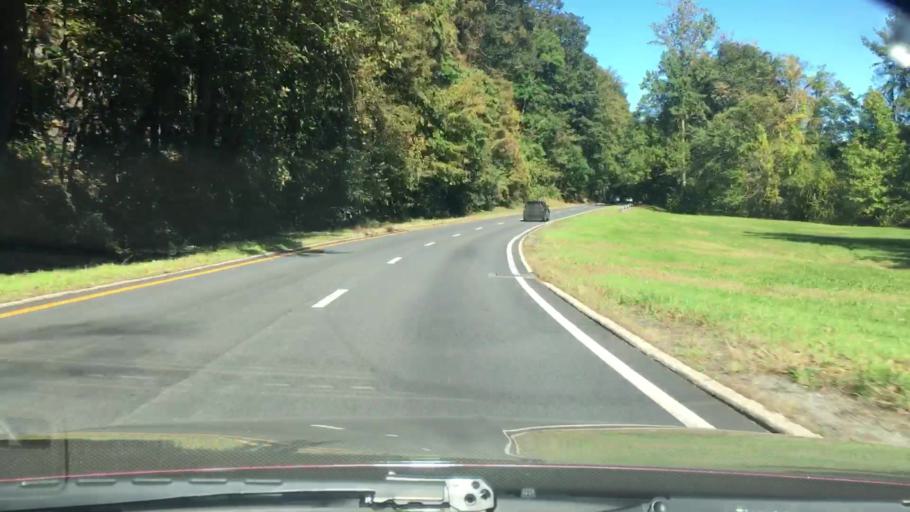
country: US
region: New York
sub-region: Westchester County
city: Chappaqua
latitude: 41.1695
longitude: -73.7671
